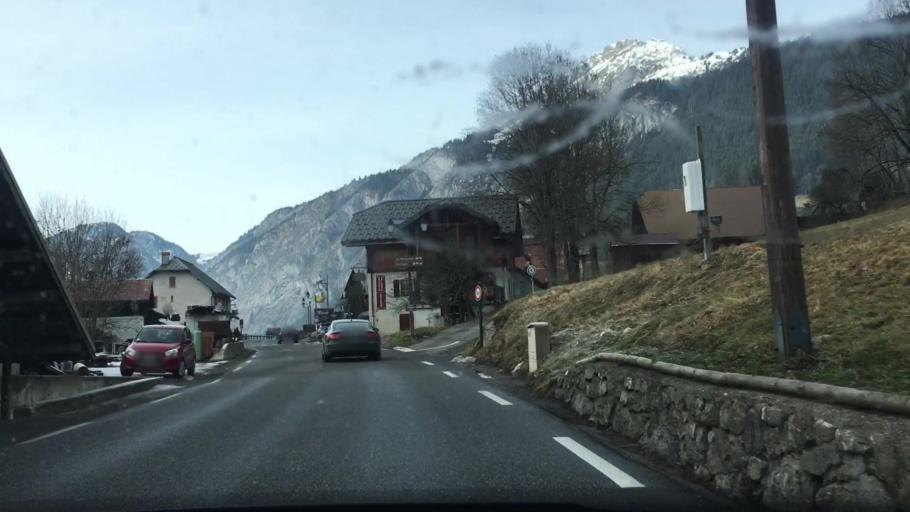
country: FR
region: Rhone-Alpes
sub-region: Departement de la Haute-Savoie
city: Chatel
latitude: 46.2934
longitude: 6.7958
